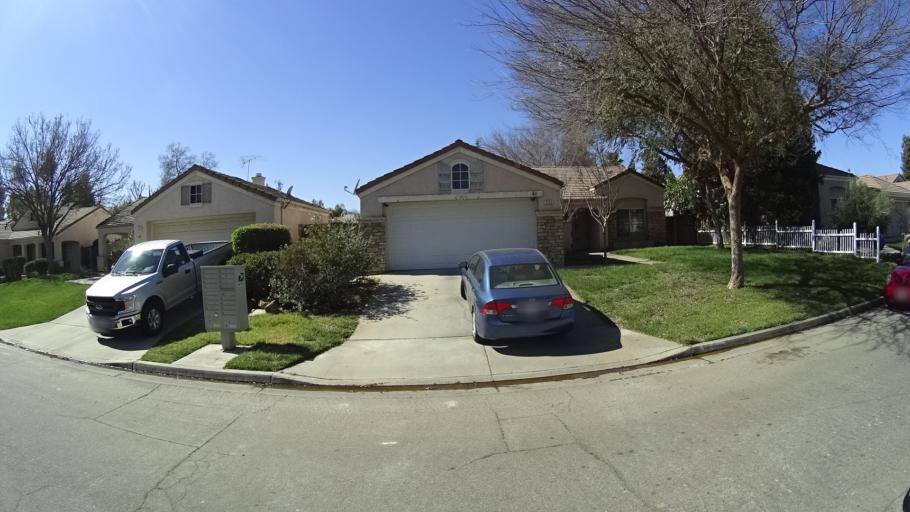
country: US
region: California
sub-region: Fresno County
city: Clovis
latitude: 36.8486
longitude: -119.7428
